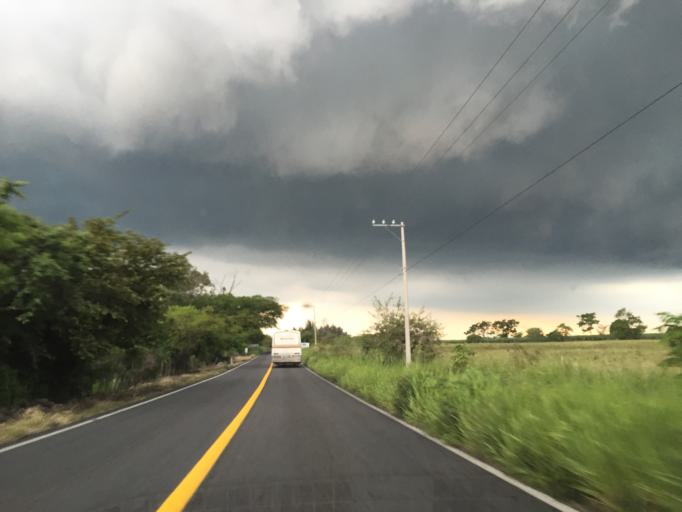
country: MX
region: Colima
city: Cuauhtemoc
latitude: 19.3421
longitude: -103.5855
